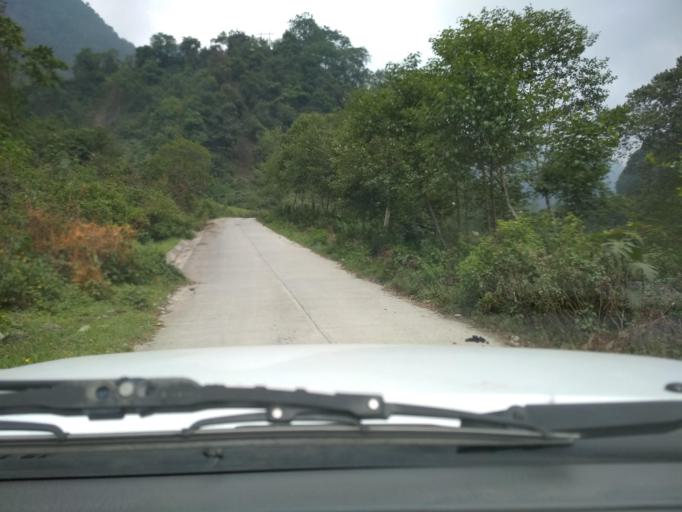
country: MX
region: Veracruz
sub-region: La Perla
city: Metlac Hernandez (Metlac Primero)
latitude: 18.9819
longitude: -97.1342
